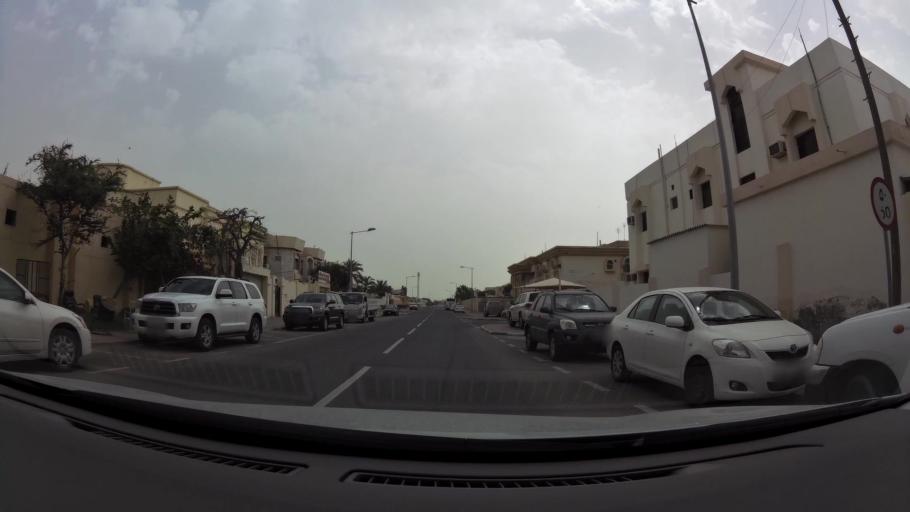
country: QA
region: Baladiyat ad Dawhah
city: Doha
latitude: 25.2564
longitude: 51.5249
